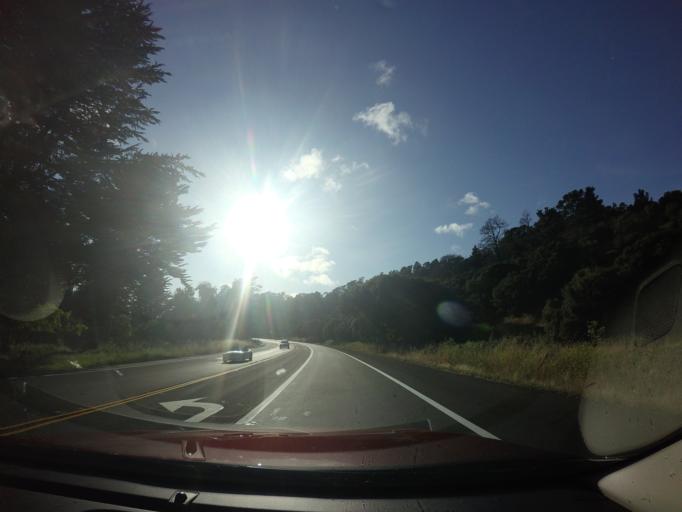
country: US
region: California
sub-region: Monterey County
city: Carmel-by-the-Sea
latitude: 36.5403
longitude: -121.8654
